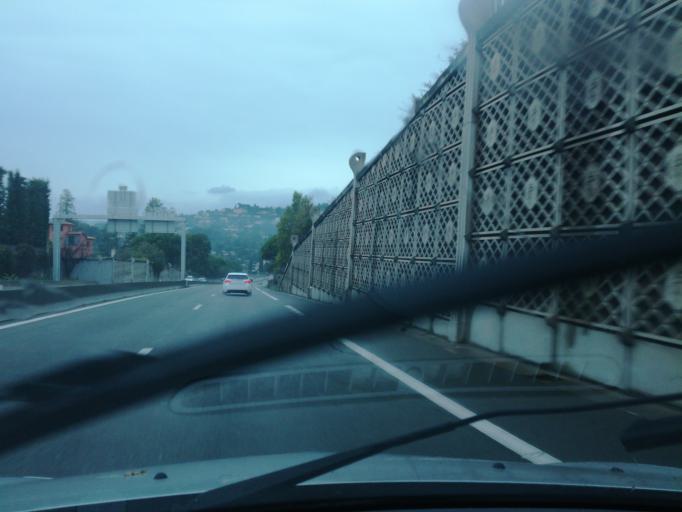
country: FR
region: Provence-Alpes-Cote d'Azur
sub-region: Departement des Alpes-Maritimes
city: Mougins
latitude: 43.5876
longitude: 7.0041
